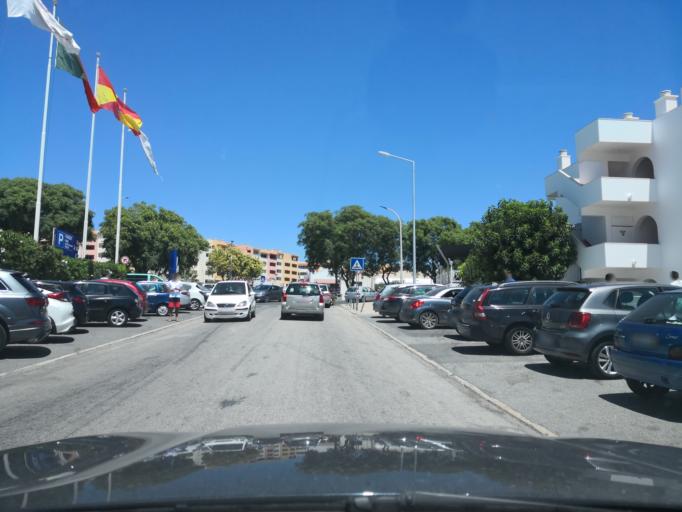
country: PT
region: Faro
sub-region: Albufeira
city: Albufeira
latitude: 37.0908
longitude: -8.2408
